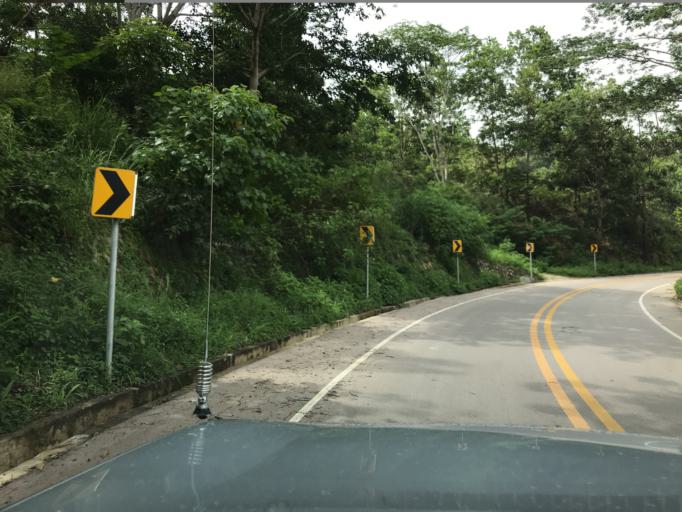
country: TL
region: Aileu
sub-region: Aileu Villa
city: Aileu
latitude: -8.7204
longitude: 125.5641
